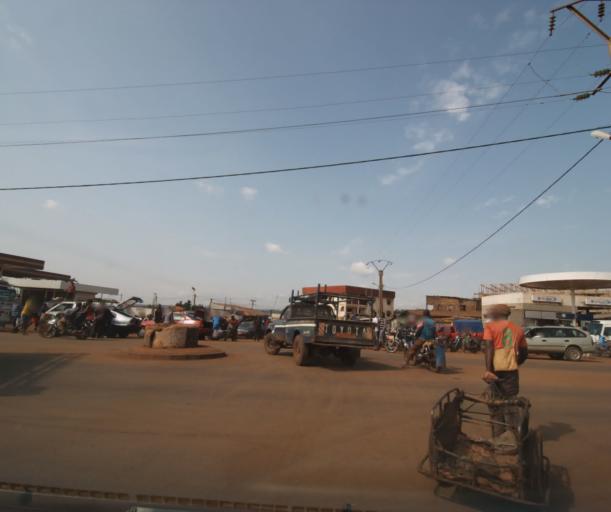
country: CM
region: West
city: Mbouda
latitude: 5.6268
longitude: 10.2584
